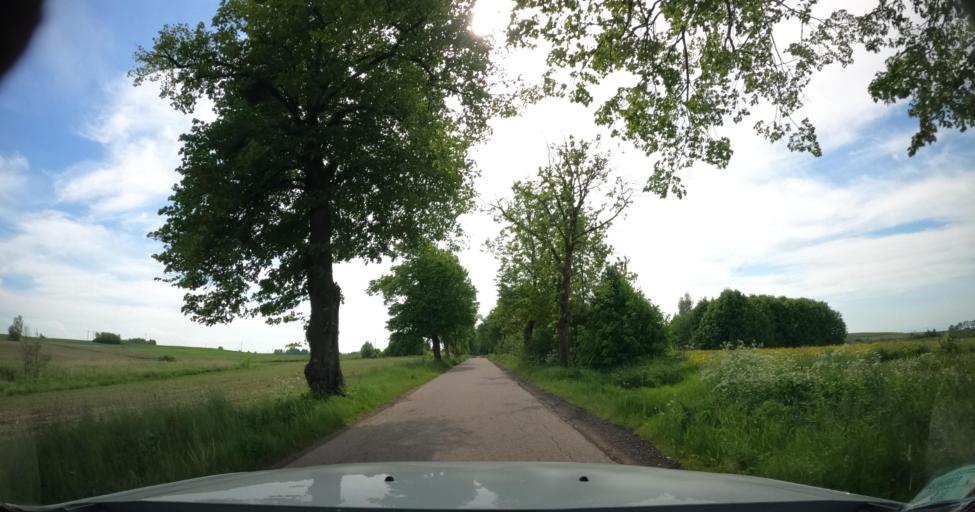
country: PL
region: Warmian-Masurian Voivodeship
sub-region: Powiat lidzbarski
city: Lubomino
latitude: 54.0864
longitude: 20.2867
